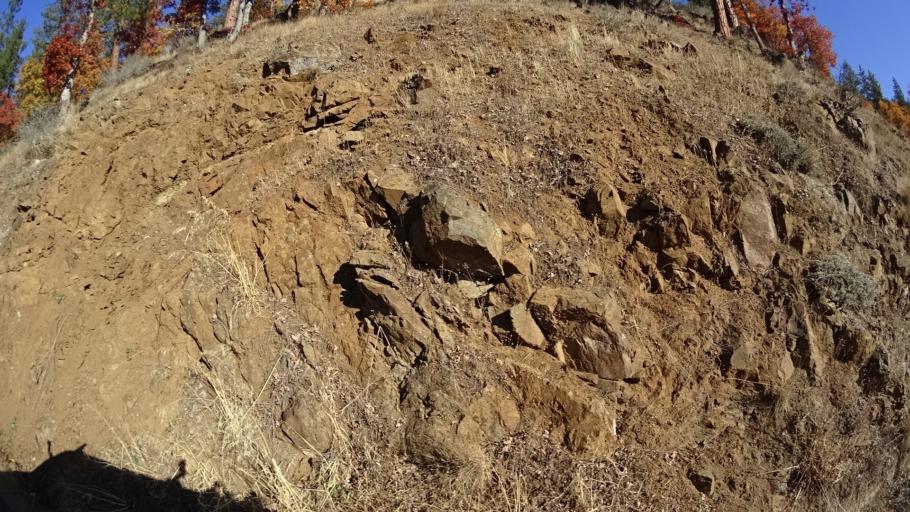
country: US
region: California
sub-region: Siskiyou County
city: Yreka
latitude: 41.6340
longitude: -122.9598
